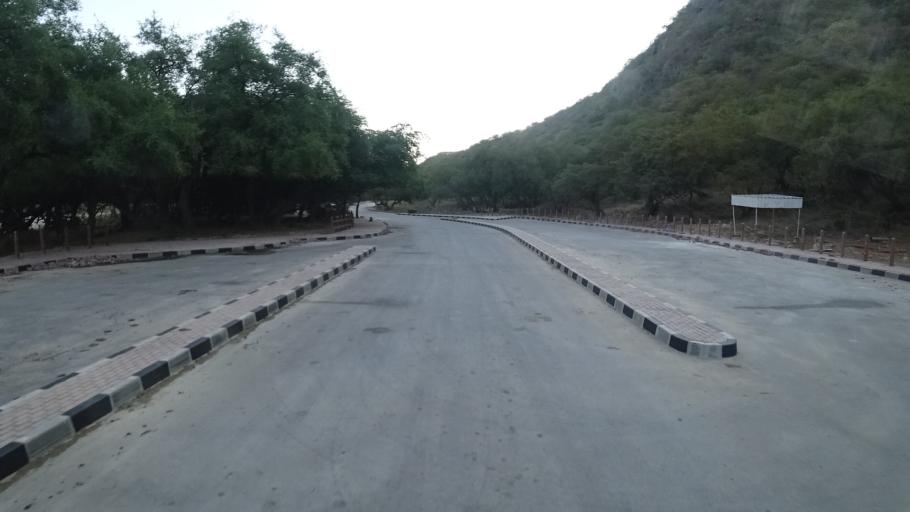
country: OM
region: Zufar
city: Salalah
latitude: 17.1044
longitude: 54.4526
